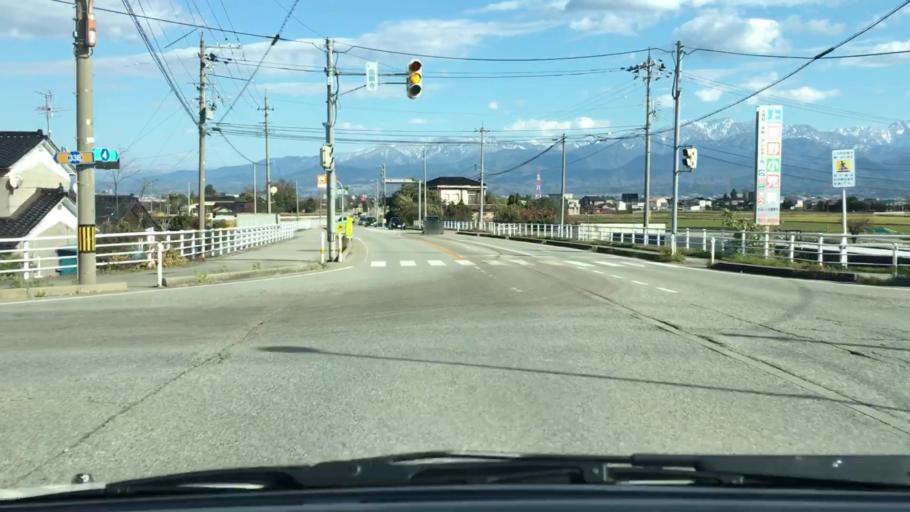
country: JP
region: Toyama
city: Toyama-shi
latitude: 36.7041
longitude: 137.2794
